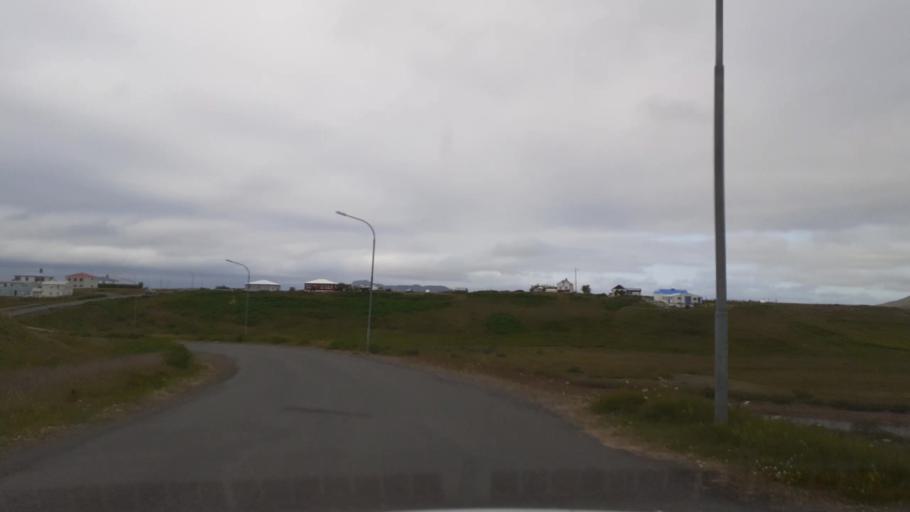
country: IS
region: Northwest
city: Saudarkrokur
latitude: 65.8981
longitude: -19.4120
